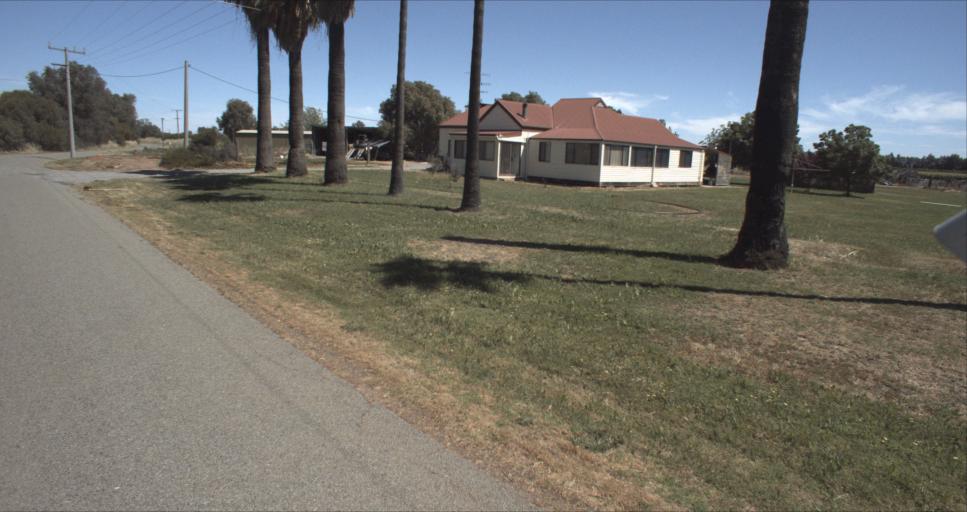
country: AU
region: New South Wales
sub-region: Leeton
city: Leeton
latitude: -34.5262
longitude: 146.3460
